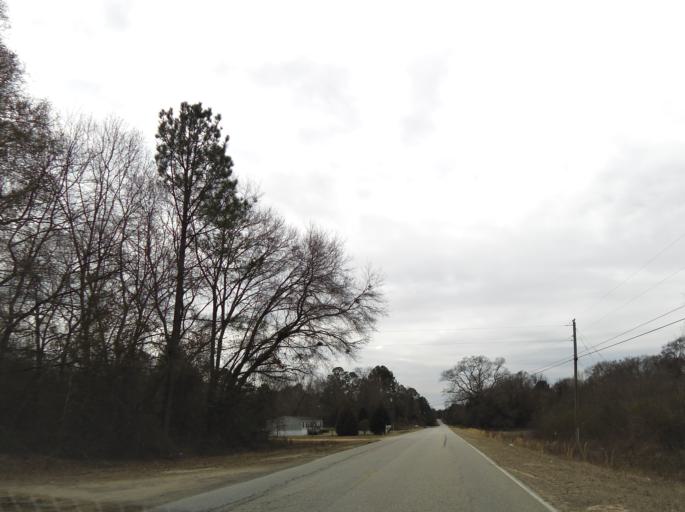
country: US
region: Georgia
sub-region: Peach County
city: Byron
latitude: 32.6139
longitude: -83.7873
